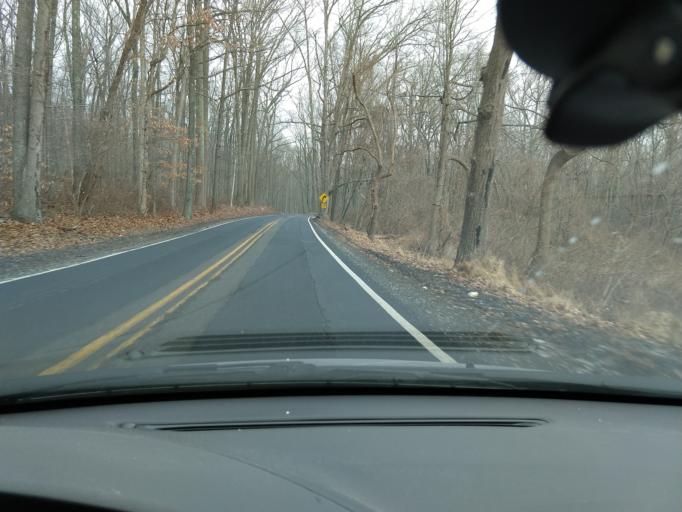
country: US
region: Pennsylvania
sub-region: Chester County
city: Elverson
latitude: 40.1970
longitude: -75.7730
